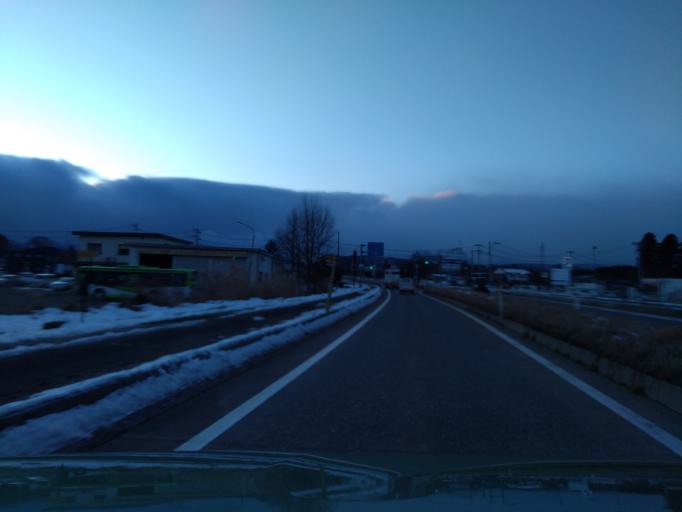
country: JP
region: Iwate
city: Shizukuishi
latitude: 39.7028
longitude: 140.9714
